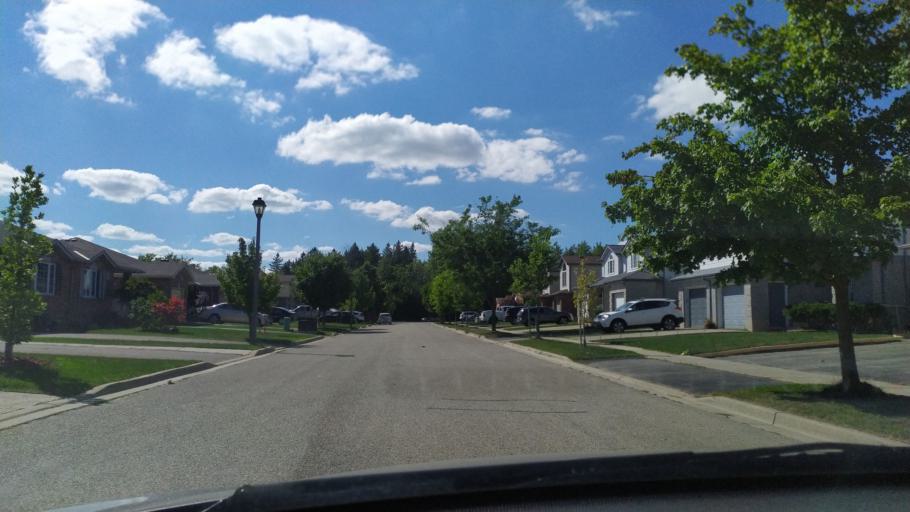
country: CA
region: Ontario
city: Stratford
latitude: 43.3547
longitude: -80.9888
